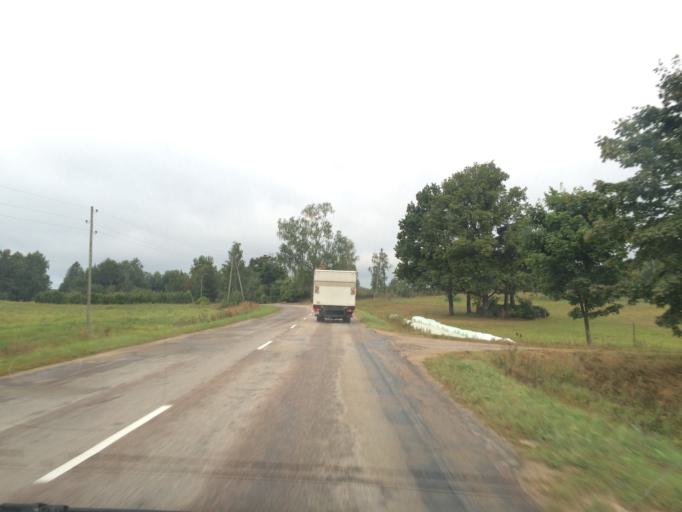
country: LV
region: Ikskile
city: Ikskile
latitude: 56.8558
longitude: 24.5227
